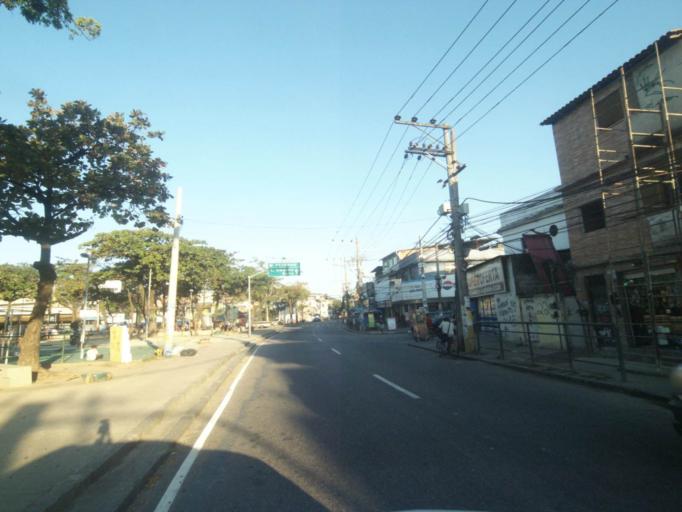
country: BR
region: Rio de Janeiro
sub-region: Sao Joao De Meriti
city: Sao Joao de Meriti
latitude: -22.9472
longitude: -43.3607
